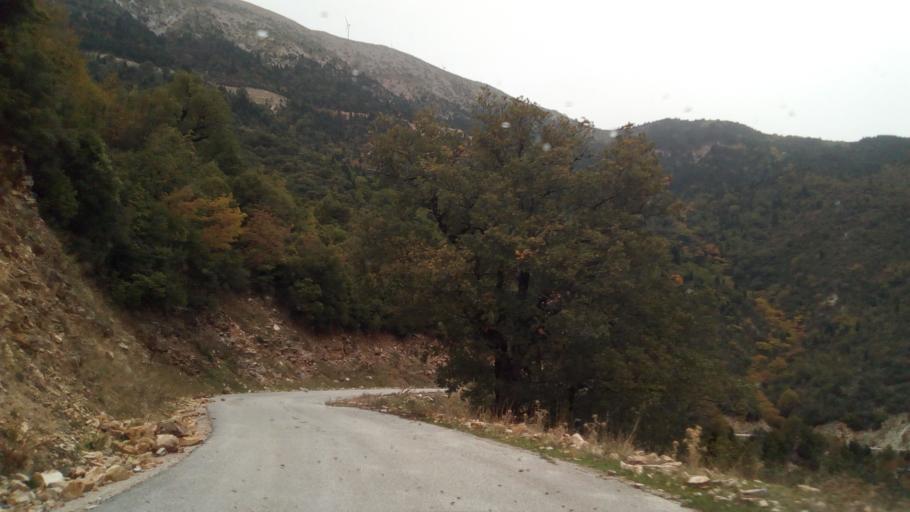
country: GR
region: West Greece
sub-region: Nomos Aitolias kai Akarnanias
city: Thermo
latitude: 38.6117
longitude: 21.8284
